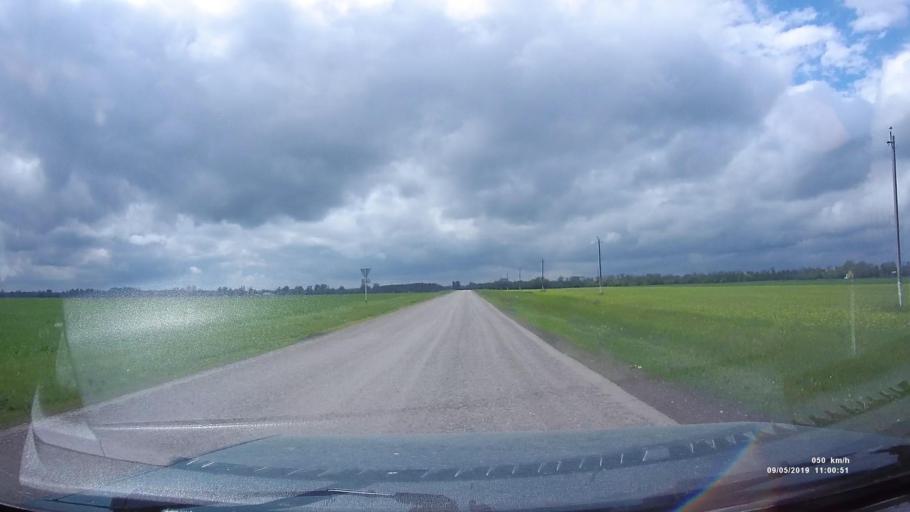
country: RU
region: Rostov
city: Peshkovo
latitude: 46.8514
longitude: 39.2167
